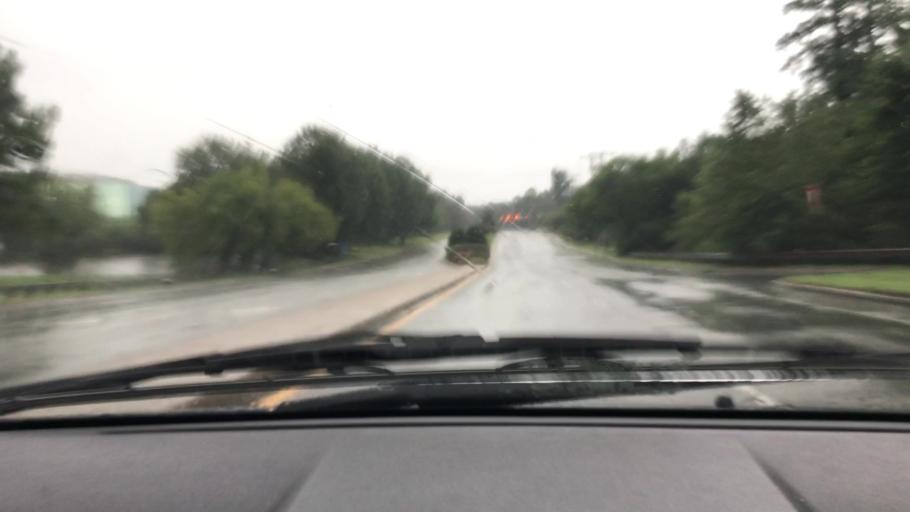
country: US
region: Virginia
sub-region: Henrico County
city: Short Pump
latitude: 37.6650
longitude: -77.5728
